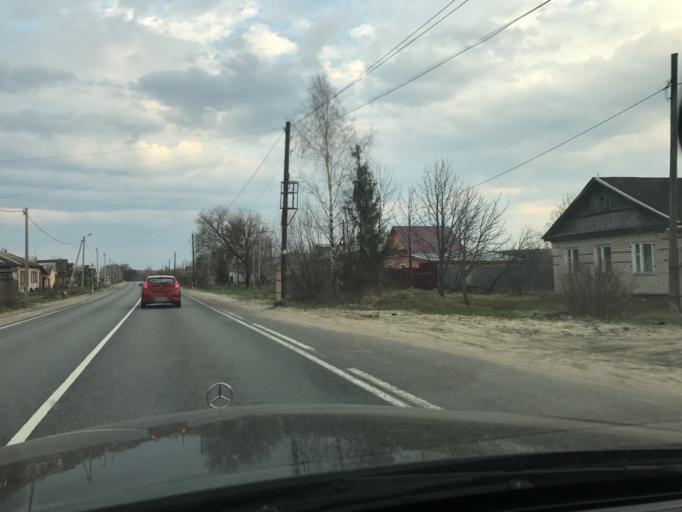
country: RU
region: Vladimir
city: Murom
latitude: 55.6463
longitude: 41.8353
